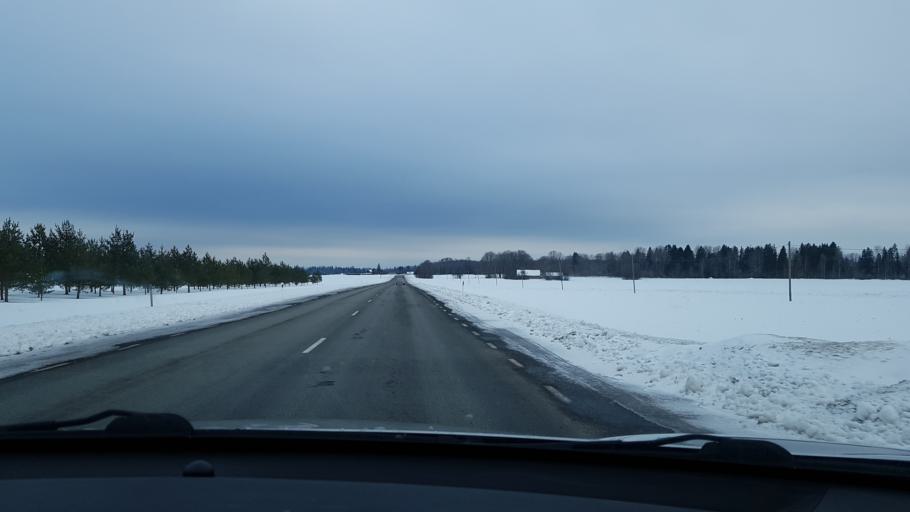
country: EE
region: Jaervamaa
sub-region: Paide linn
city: Paide
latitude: 58.8880
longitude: 25.7116
